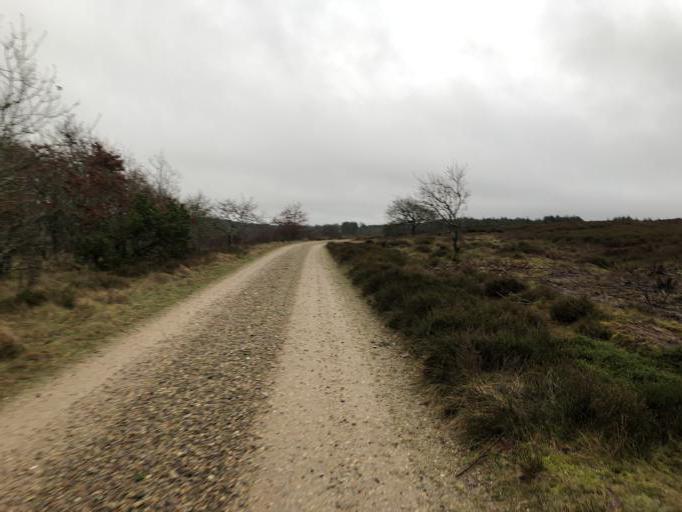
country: DK
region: Central Jutland
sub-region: Holstebro Kommune
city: Ulfborg
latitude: 56.2851
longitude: 8.4619
